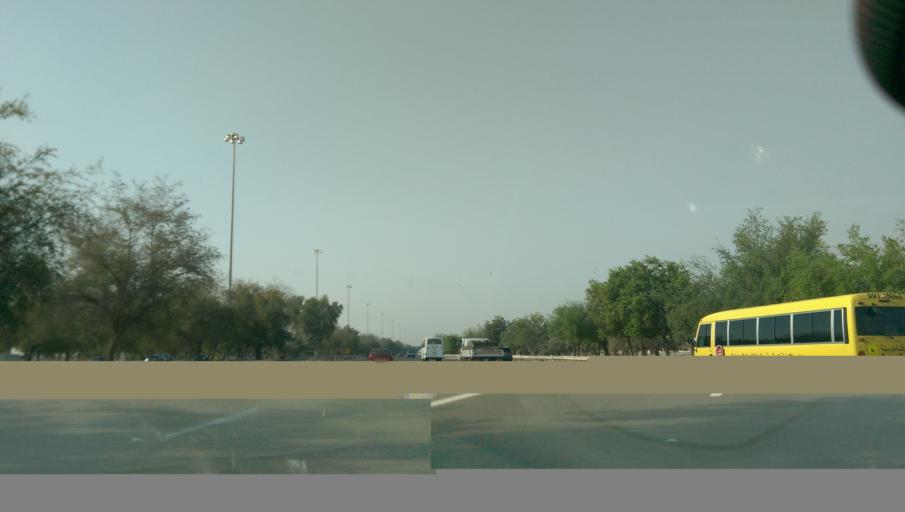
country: AE
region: Abu Dhabi
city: Abu Dhabi
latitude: 24.4525
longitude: 54.6785
